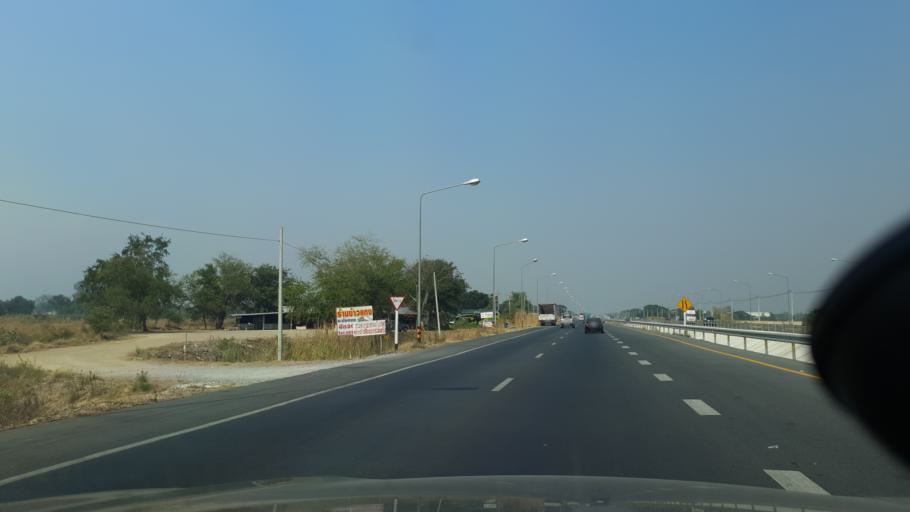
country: TH
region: Nakhon Sawan
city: Krok Phra
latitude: 15.6240
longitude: 100.1118
